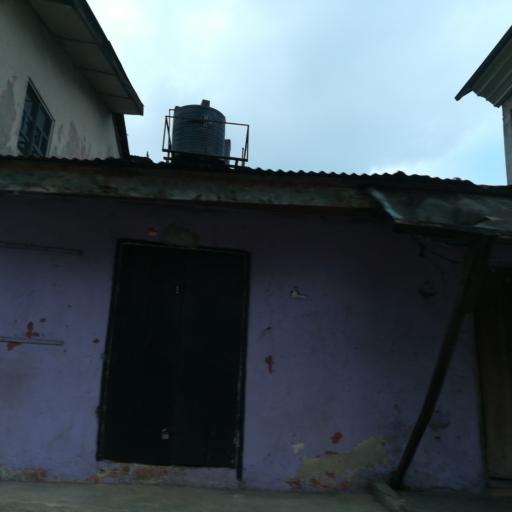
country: NG
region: Rivers
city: Port Harcourt
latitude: 4.8090
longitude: 7.0500
